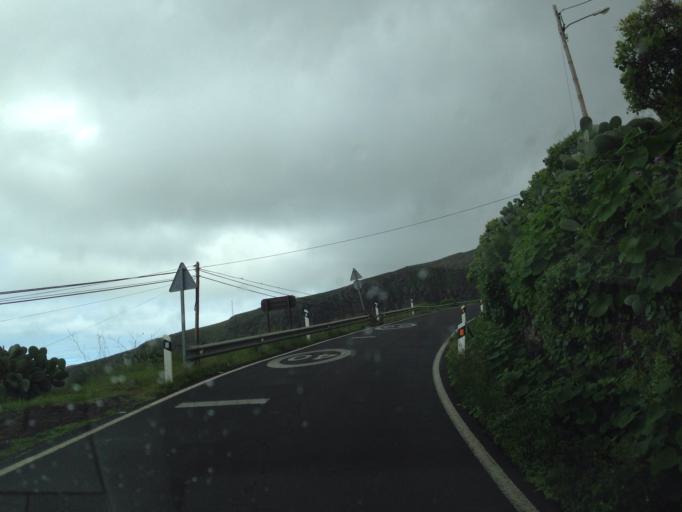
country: ES
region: Canary Islands
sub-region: Provincia de Las Palmas
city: Guia
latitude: 28.1169
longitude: -15.6470
